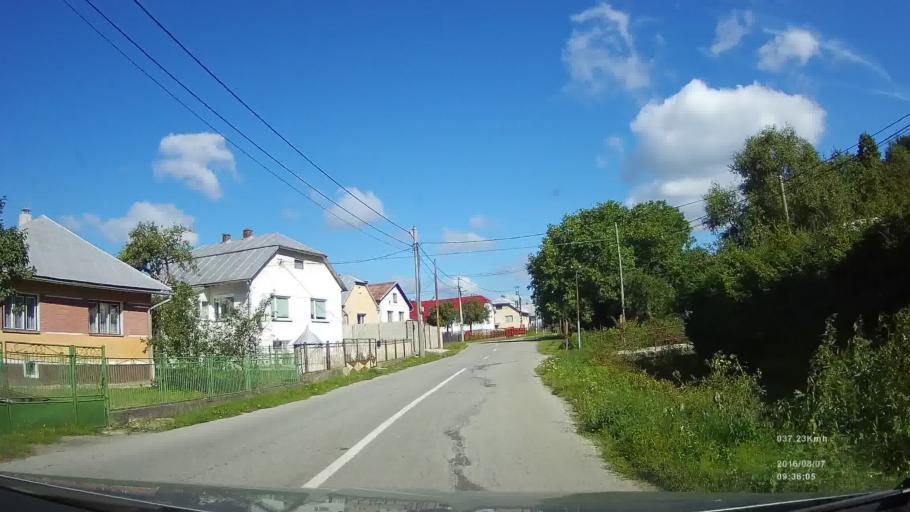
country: PL
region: Subcarpathian Voivodeship
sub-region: Powiat krosnienski
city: Jasliska
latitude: 49.3263
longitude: 21.7341
